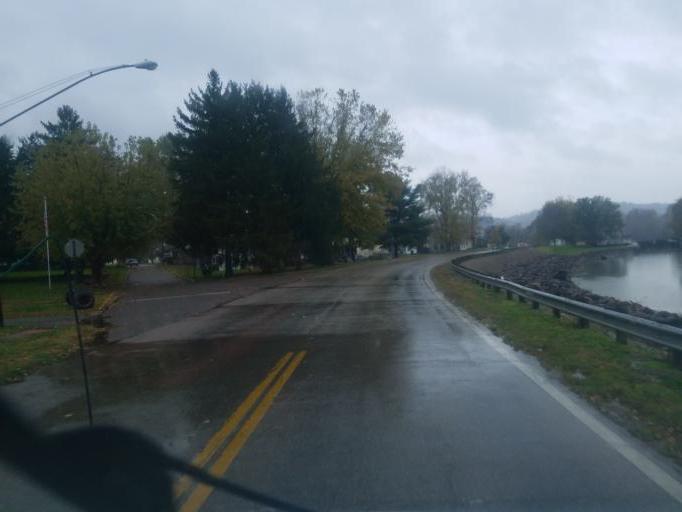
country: US
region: Ohio
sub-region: Morgan County
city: McConnelsville
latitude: 39.6448
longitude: -81.8479
